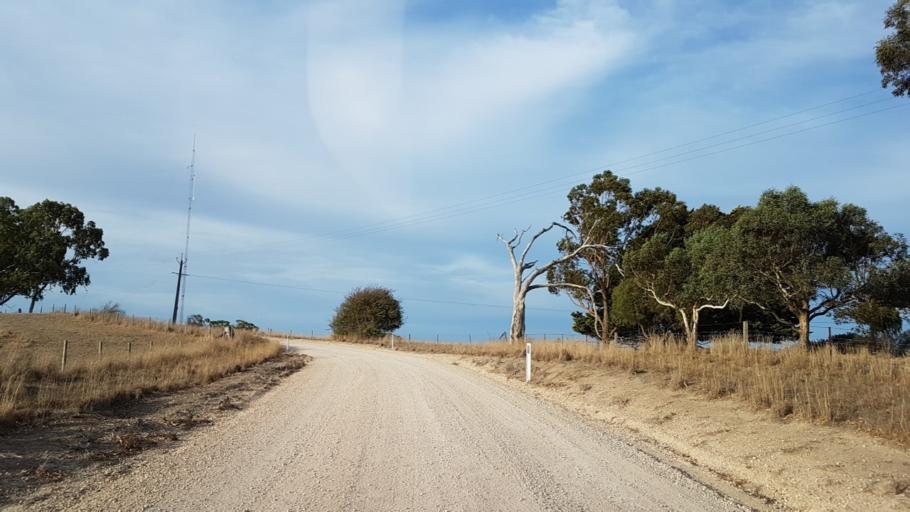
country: AU
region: South Australia
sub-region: Mount Barker
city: Nairne
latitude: -35.0083
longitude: 138.9115
